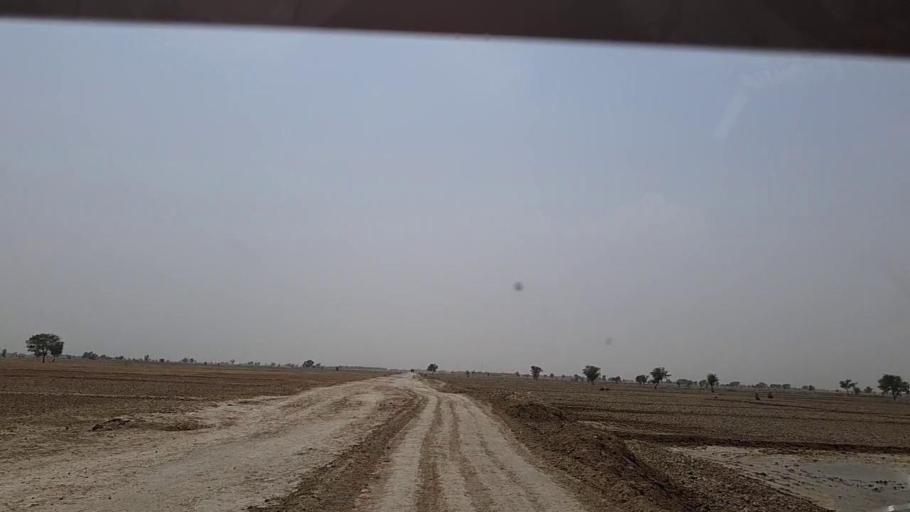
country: PK
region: Sindh
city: Khairpur Nathan Shah
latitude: 27.0189
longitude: 67.6199
